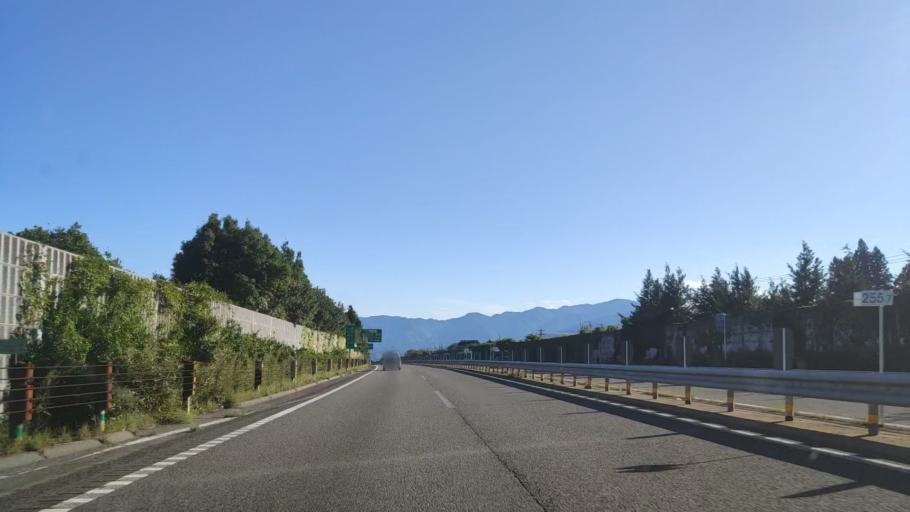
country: JP
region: Nagano
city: Iida
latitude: 35.4762
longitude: 137.7602
